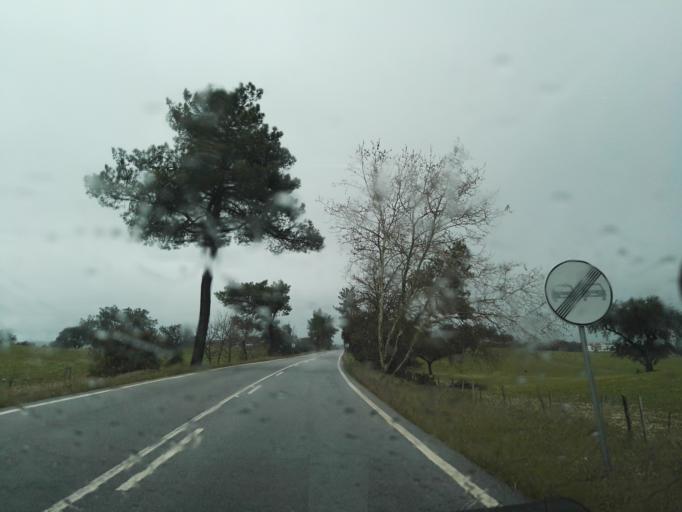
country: PT
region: Portalegre
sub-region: Arronches
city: Arronches
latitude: 39.0802
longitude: -7.2809
